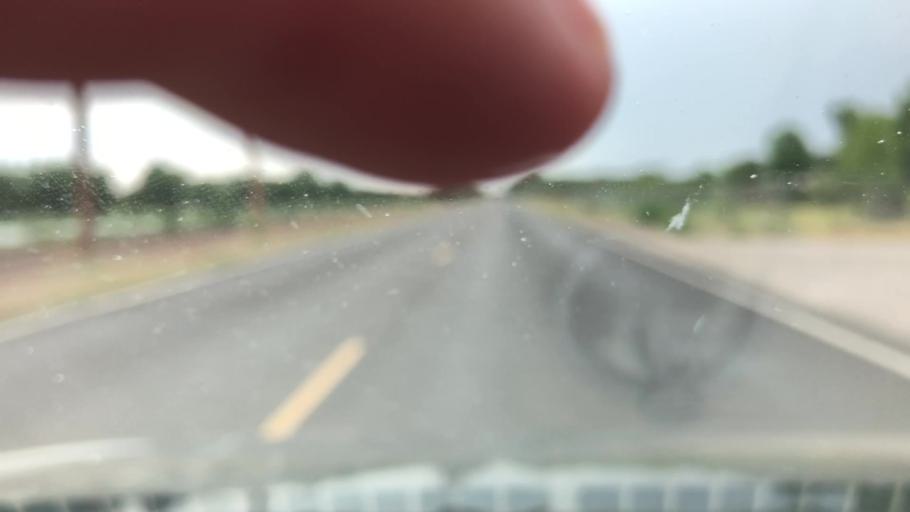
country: US
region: Texas
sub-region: El Paso County
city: Canutillo
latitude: 31.9222
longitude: -106.6271
